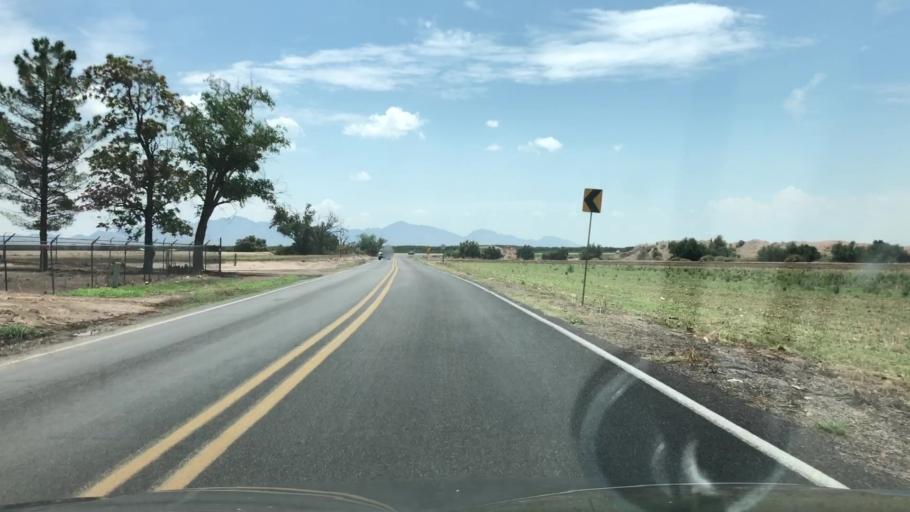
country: US
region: New Mexico
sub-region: Dona Ana County
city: Vado
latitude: 32.0706
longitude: -106.6827
